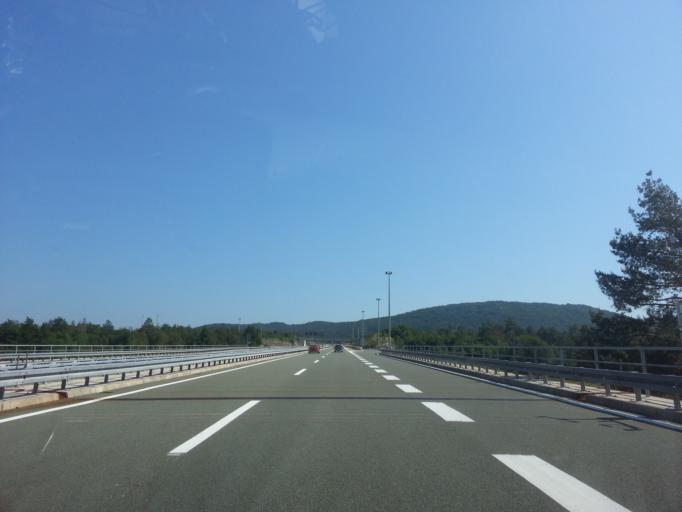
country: HR
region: Primorsko-Goranska
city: Klana
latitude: 45.4692
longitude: 14.2730
